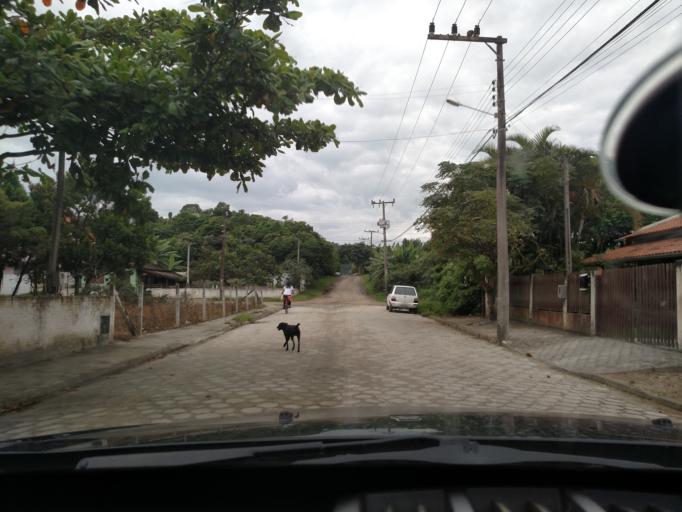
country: BR
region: Santa Catarina
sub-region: Porto Belo
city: Porto Belo
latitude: -27.1509
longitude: -48.5085
